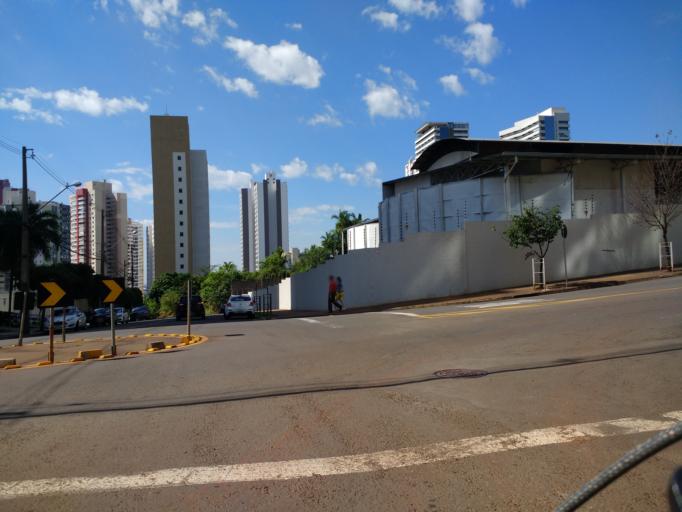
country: BR
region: Parana
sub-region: Londrina
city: Londrina
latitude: -23.3336
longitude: -51.1802
